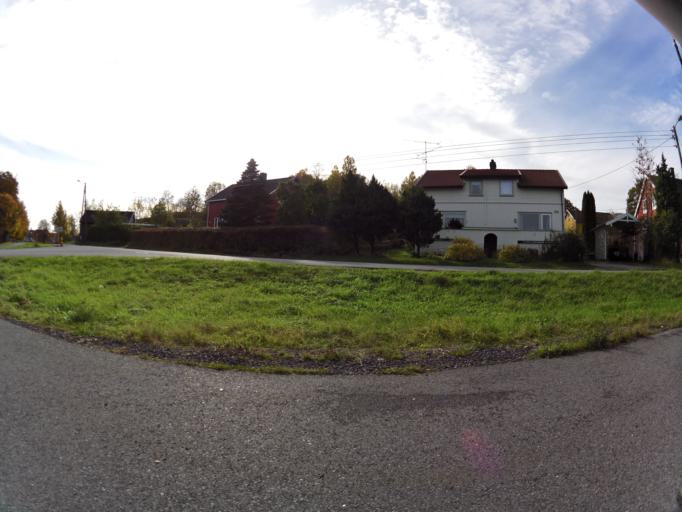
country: NO
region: Ostfold
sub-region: Fredrikstad
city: Fredrikstad
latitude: 59.2390
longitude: 10.9745
